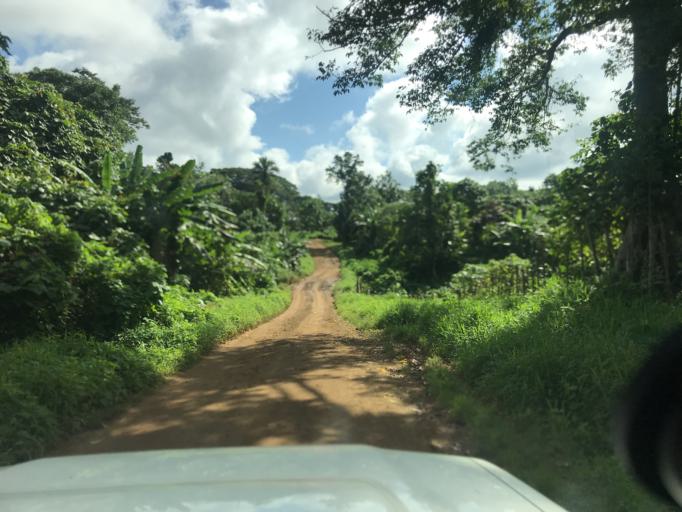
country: VU
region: Sanma
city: Luganville
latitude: -15.4835
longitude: 167.0896
